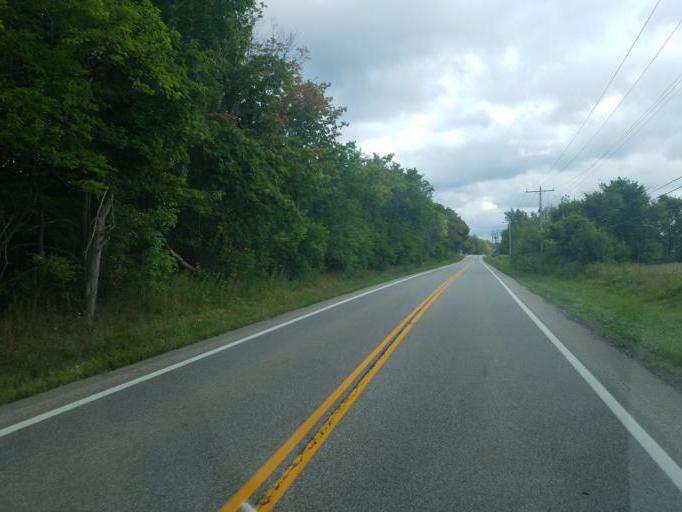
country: US
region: Ohio
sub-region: Geauga County
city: Chardon
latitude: 41.6583
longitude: -81.1162
